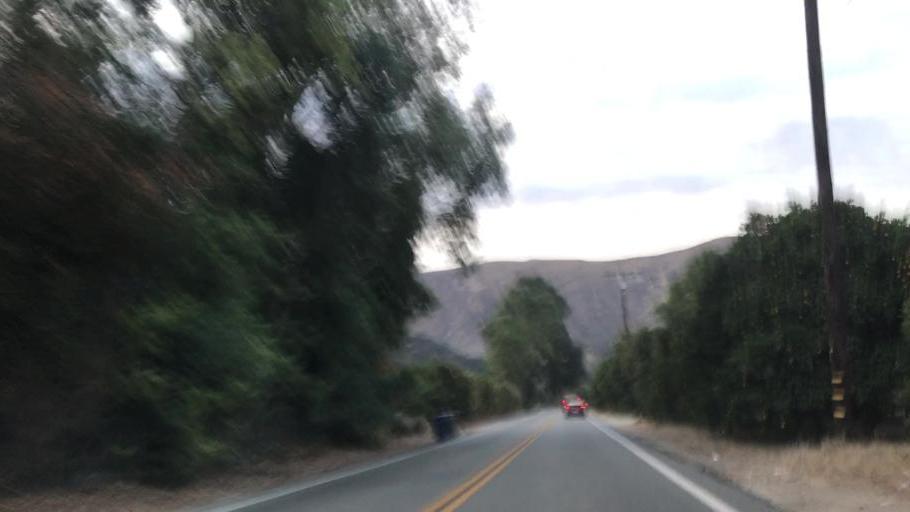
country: US
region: California
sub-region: Ventura County
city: Fillmore
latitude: 34.3663
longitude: -118.9421
